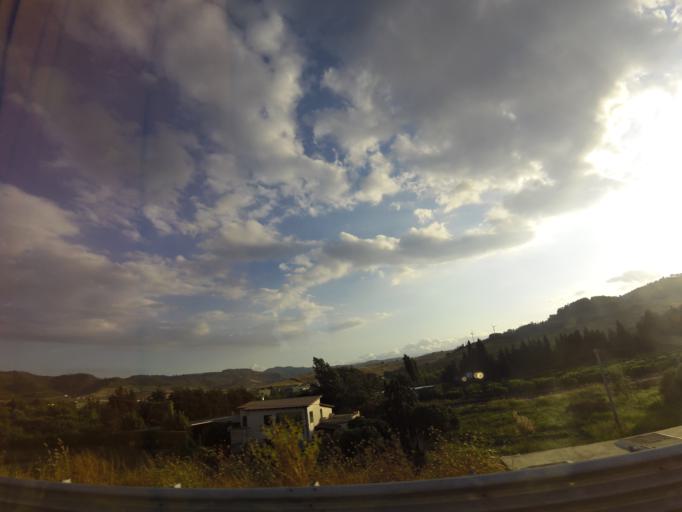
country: IT
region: Calabria
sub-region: Provincia di Catanzaro
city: Catanzaro
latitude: 38.8718
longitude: 16.5605
